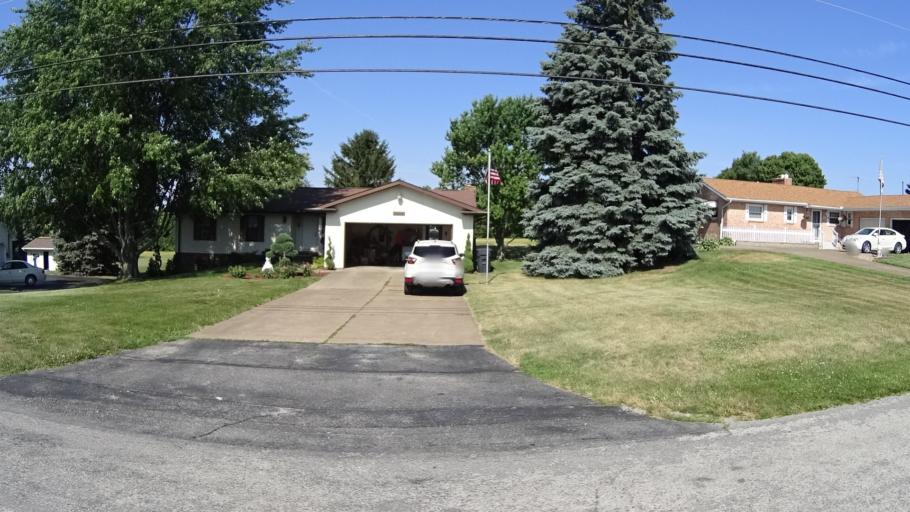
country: US
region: Ohio
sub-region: Erie County
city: Sandusky
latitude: 41.3918
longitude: -82.7959
